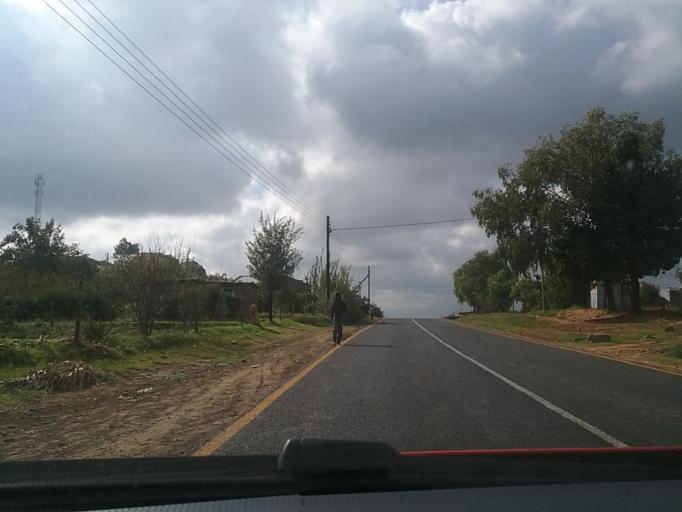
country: LS
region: Berea
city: Teyateyaneng
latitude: -29.1627
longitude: 27.7704
